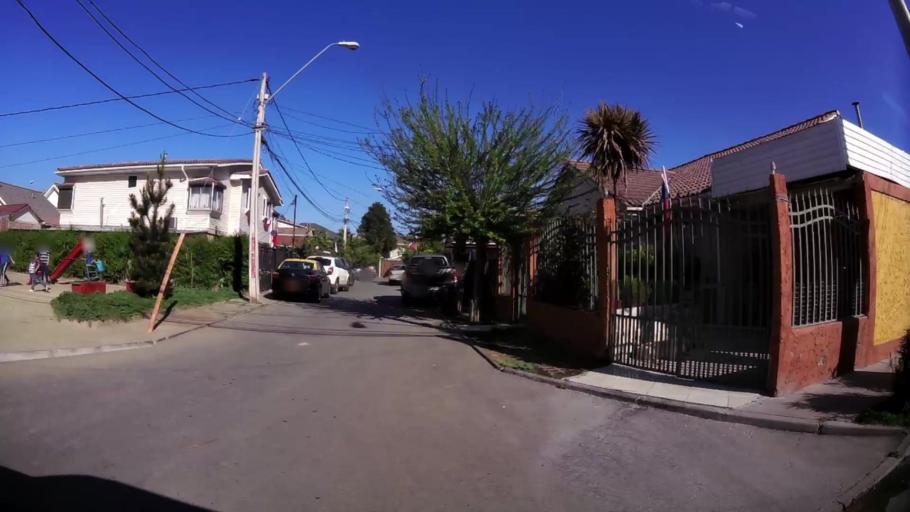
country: CL
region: Santiago Metropolitan
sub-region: Provincia de Santiago
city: Lo Prado
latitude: -33.4902
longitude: -70.7840
